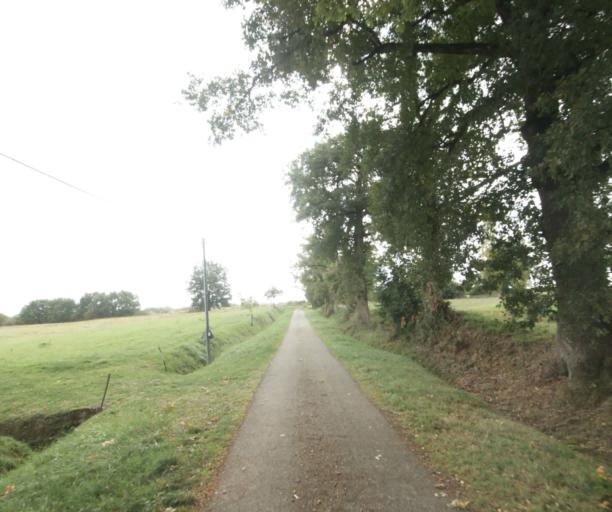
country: FR
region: Midi-Pyrenees
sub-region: Departement du Gers
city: Eauze
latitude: 43.8393
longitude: 0.1177
